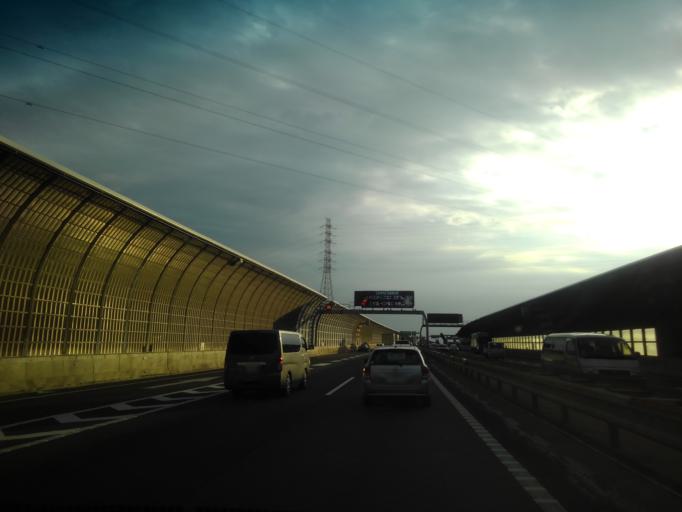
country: JP
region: Saitama
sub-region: Kawaguchi-shi
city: Hatogaya-honcho
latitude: 35.8520
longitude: 139.7262
